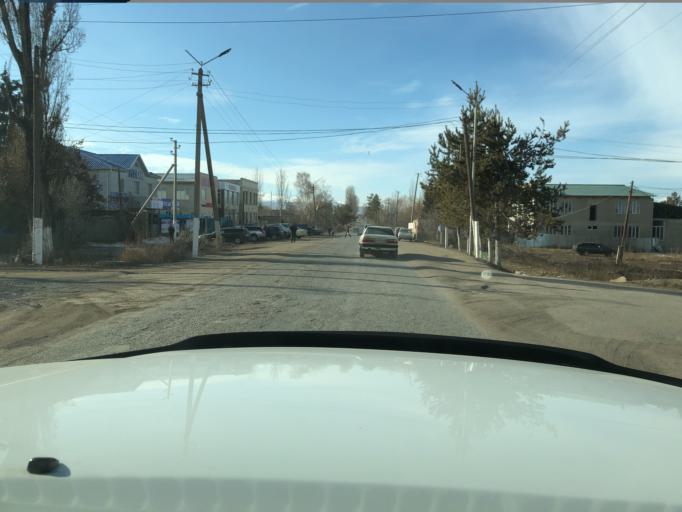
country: KG
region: Ysyk-Koel
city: Pokrovka
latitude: 42.3394
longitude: 77.9987
